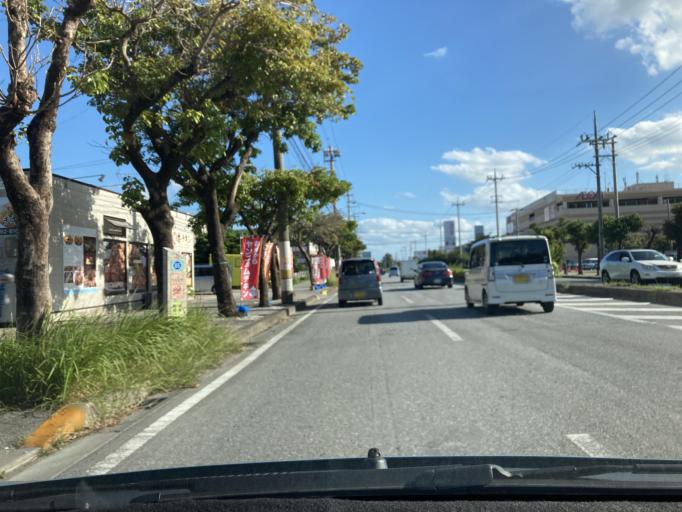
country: JP
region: Okinawa
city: Gushikawa
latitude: 26.3403
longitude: 127.8448
